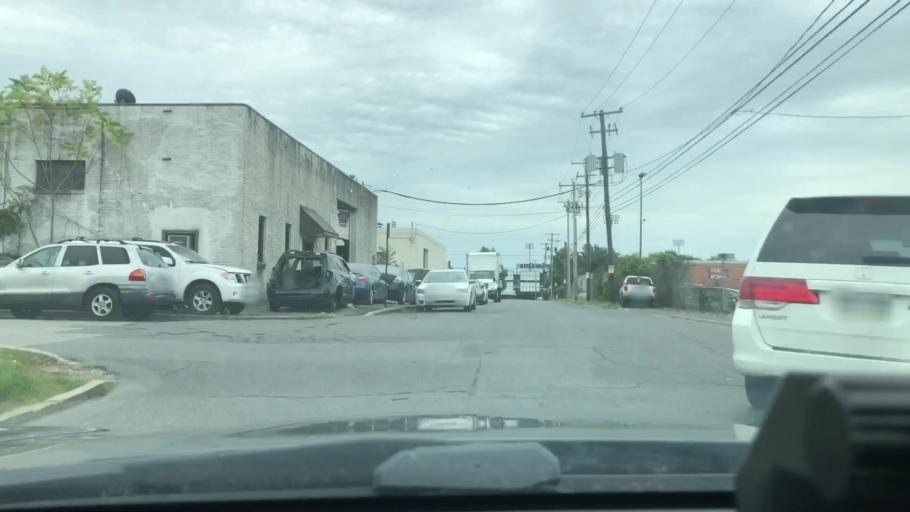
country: US
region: Pennsylvania
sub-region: Lehigh County
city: Fullerton
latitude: 40.6259
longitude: -75.4485
